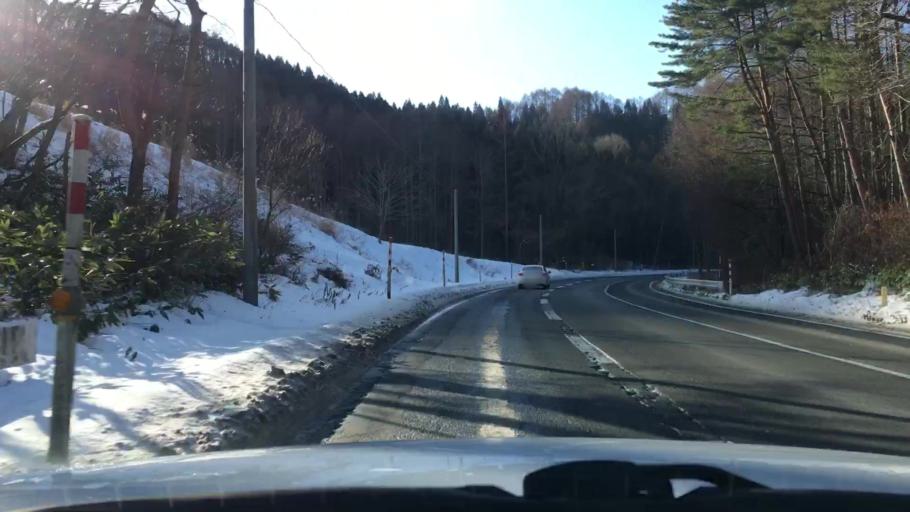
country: JP
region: Iwate
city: Morioka-shi
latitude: 39.6674
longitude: 141.3324
